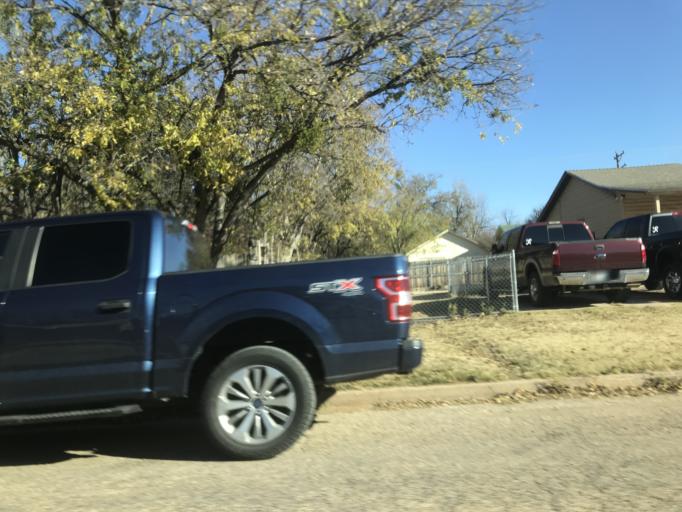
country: US
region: Texas
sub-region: Taylor County
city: Abilene
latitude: 32.4380
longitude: -99.7537
